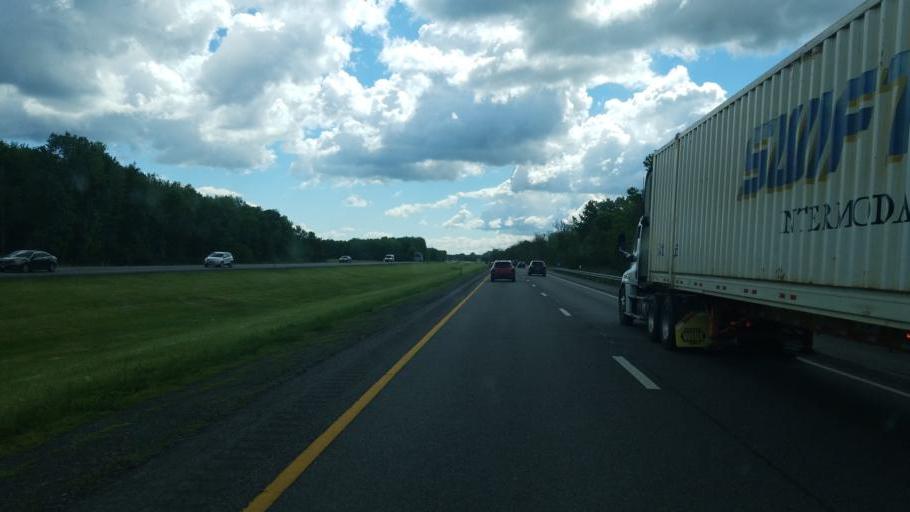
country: US
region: New York
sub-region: Madison County
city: Bolivar
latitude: 43.0912
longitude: -75.9265
